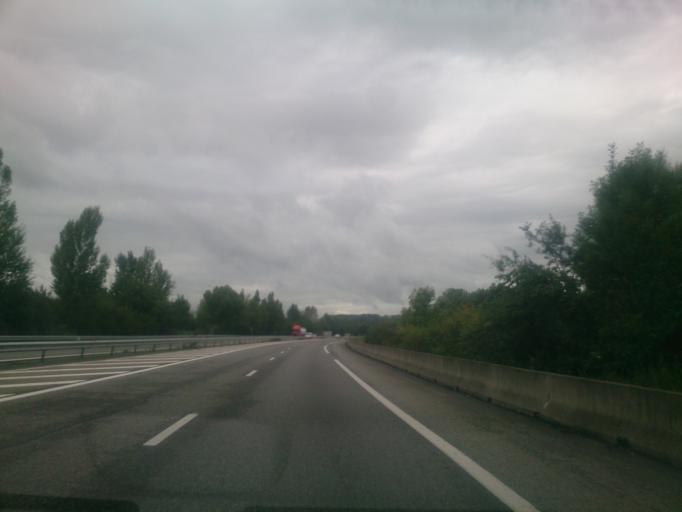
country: FR
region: Midi-Pyrenees
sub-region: Departement de la Haute-Garonne
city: Montrejeau
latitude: 43.0976
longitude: 0.5760
